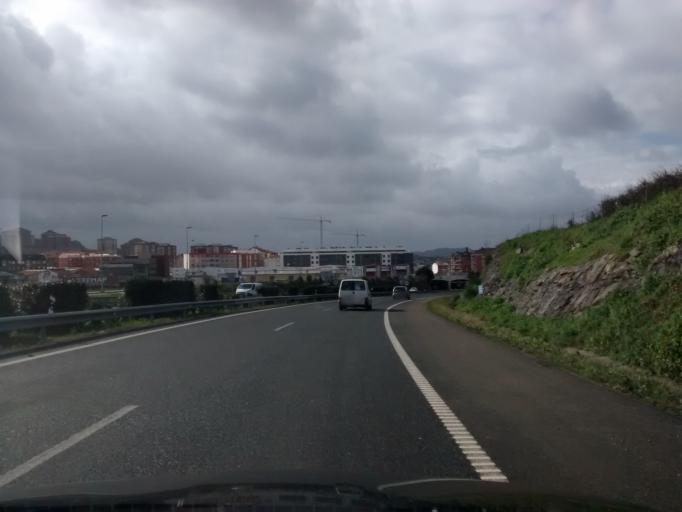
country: ES
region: Cantabria
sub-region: Provincia de Cantabria
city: Santander
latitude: 43.4657
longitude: -3.8359
